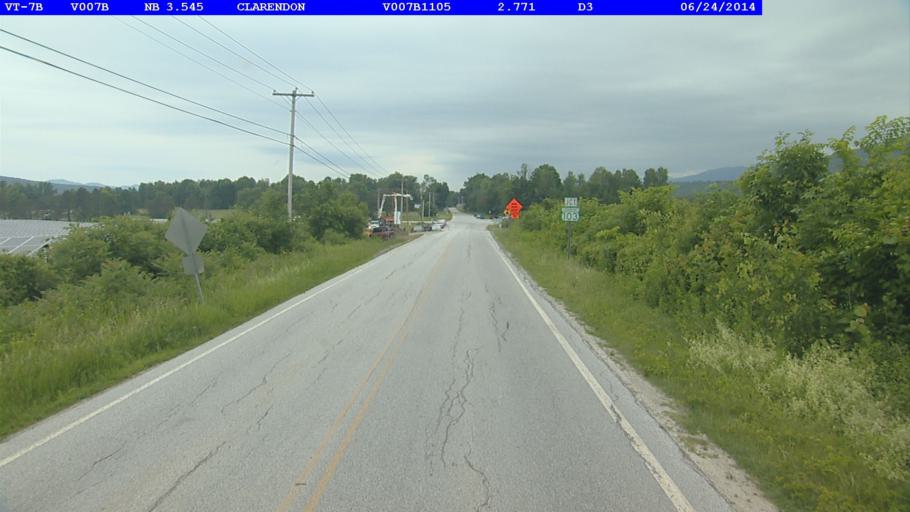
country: US
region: Vermont
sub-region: Rutland County
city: Rutland
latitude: 43.5390
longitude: -72.9537
